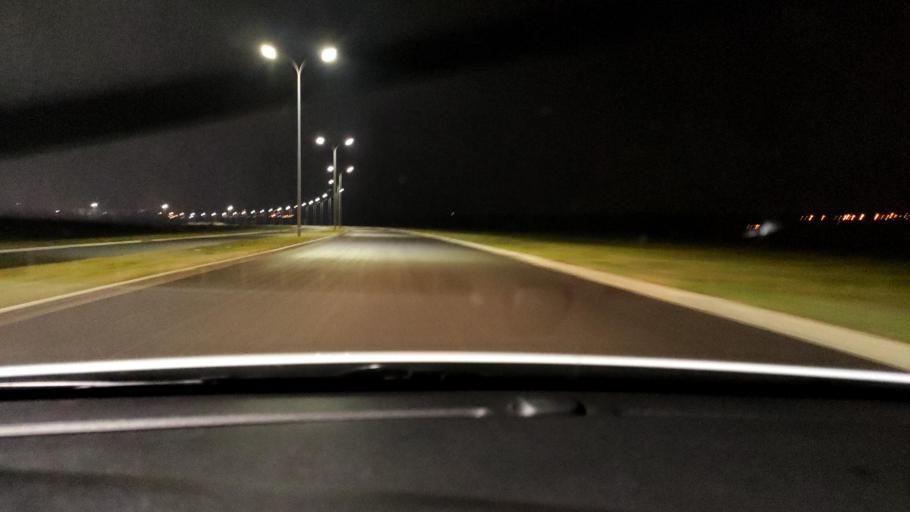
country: RU
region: Tatarstan
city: Sviyazhsk
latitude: 55.7402
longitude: 48.7439
